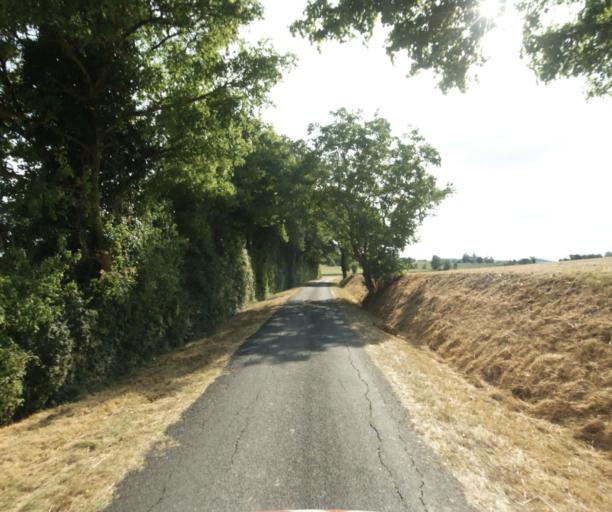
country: FR
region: Midi-Pyrenees
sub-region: Departement du Tarn
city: Puylaurens
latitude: 43.5241
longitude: 1.9938
